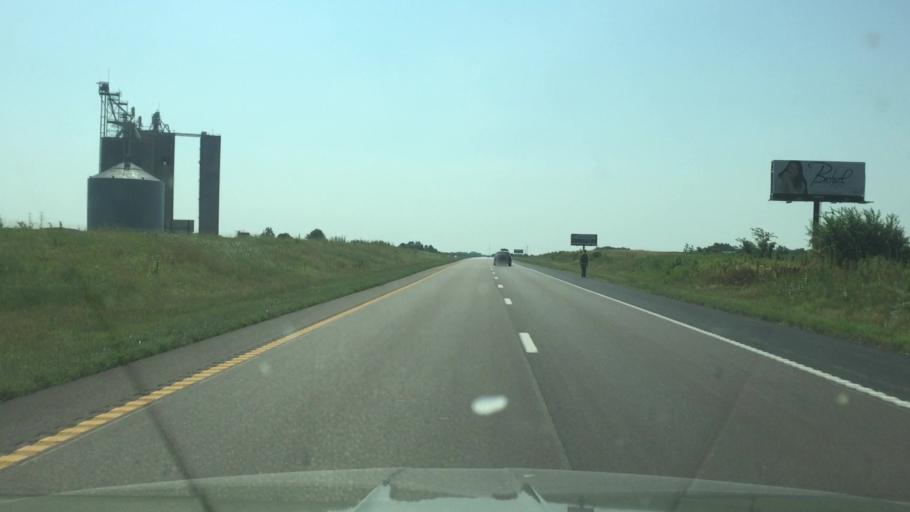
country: US
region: Missouri
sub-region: Pettis County
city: La Monte
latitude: 38.7512
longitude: -93.3505
